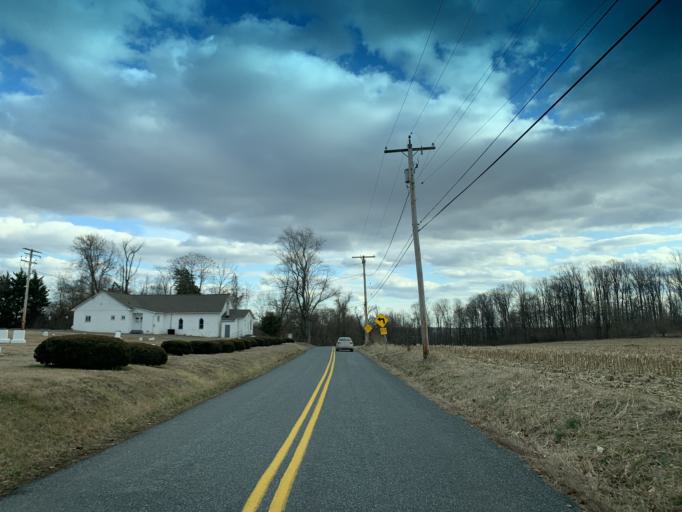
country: US
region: Maryland
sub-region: Harford County
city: South Bel Air
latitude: 39.6037
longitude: -76.3018
